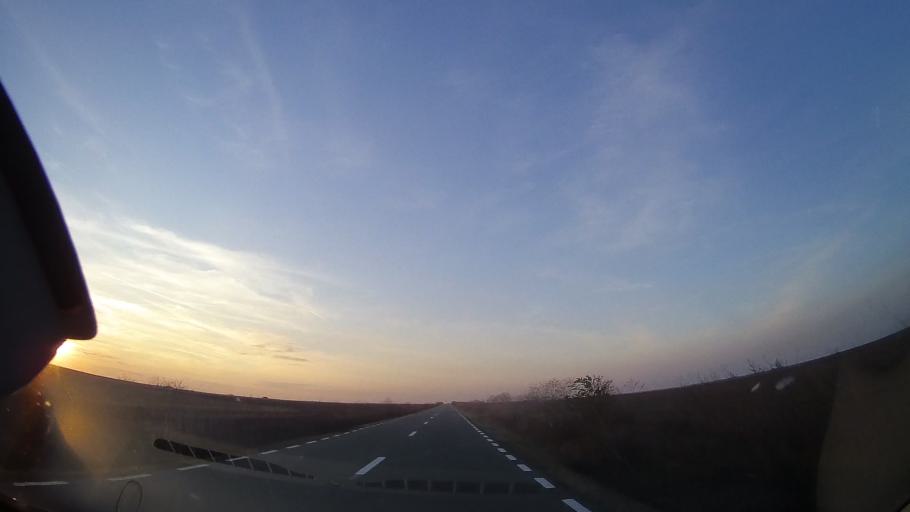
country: RO
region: Constanta
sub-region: Comuna Topraisar
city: Topraisar
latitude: 44.0215
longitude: 28.4146
